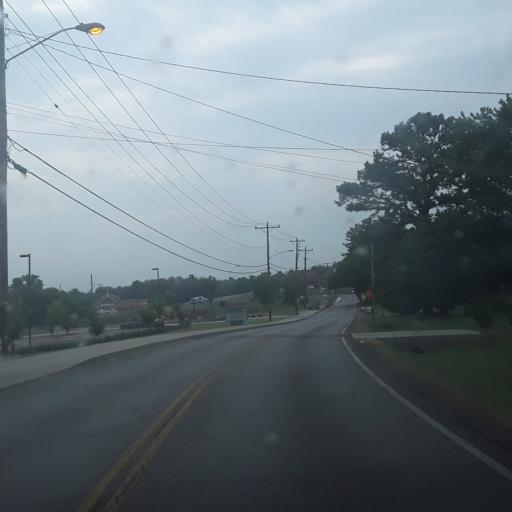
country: US
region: Tennessee
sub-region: Davidson County
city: Oak Hill
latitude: 36.0613
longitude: -86.7207
